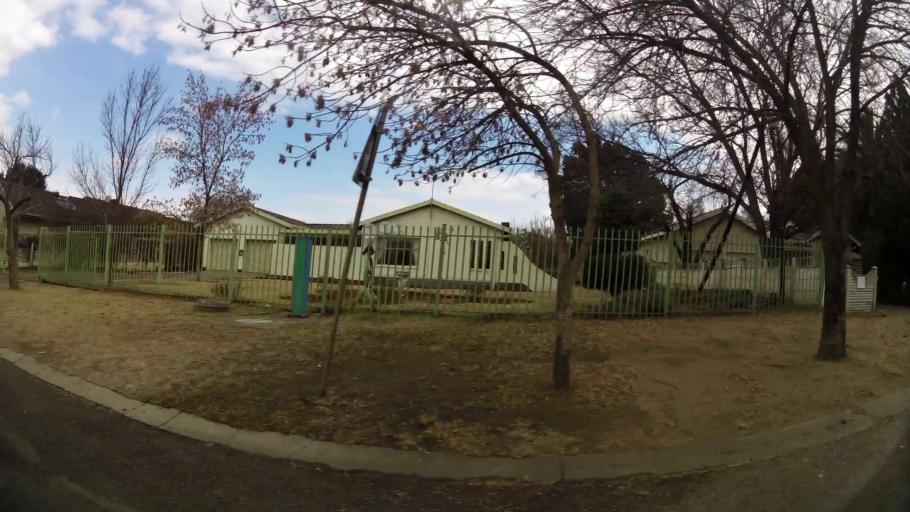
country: ZA
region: Orange Free State
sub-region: Fezile Dabi District Municipality
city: Kroonstad
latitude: -27.6434
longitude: 27.2386
